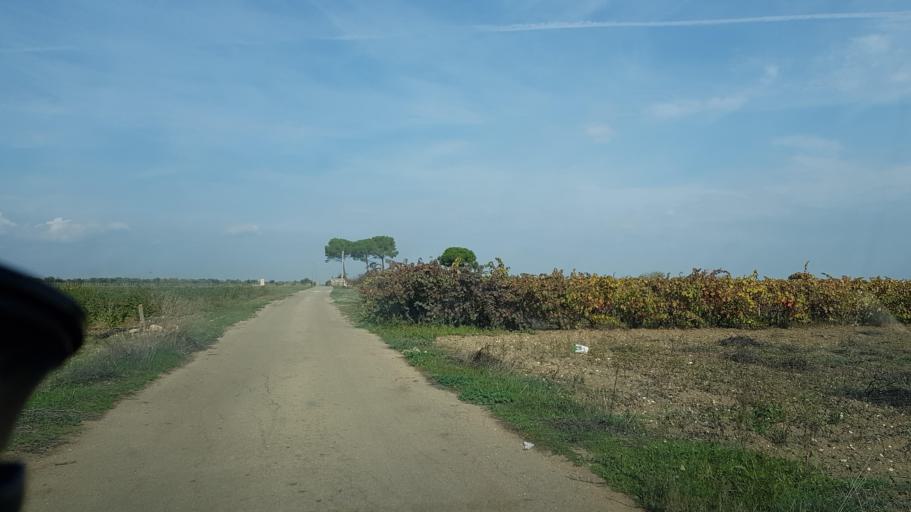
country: IT
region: Apulia
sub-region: Provincia di Brindisi
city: San Pancrazio Salentino
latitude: 40.4254
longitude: 17.8600
